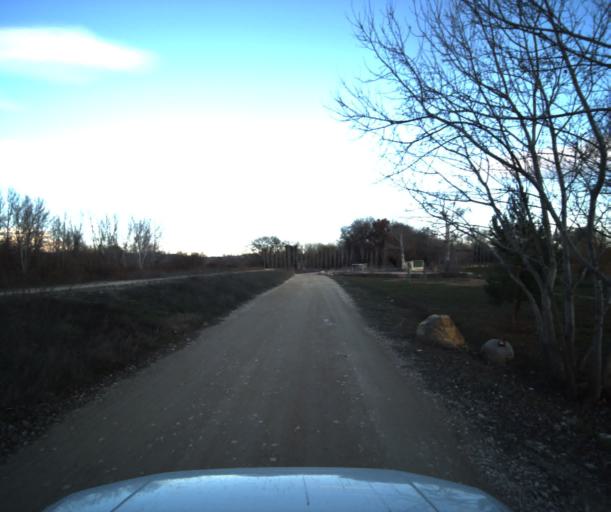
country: FR
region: Provence-Alpes-Cote d'Azur
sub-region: Departement du Vaucluse
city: Pertuis
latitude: 43.6710
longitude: 5.5018
